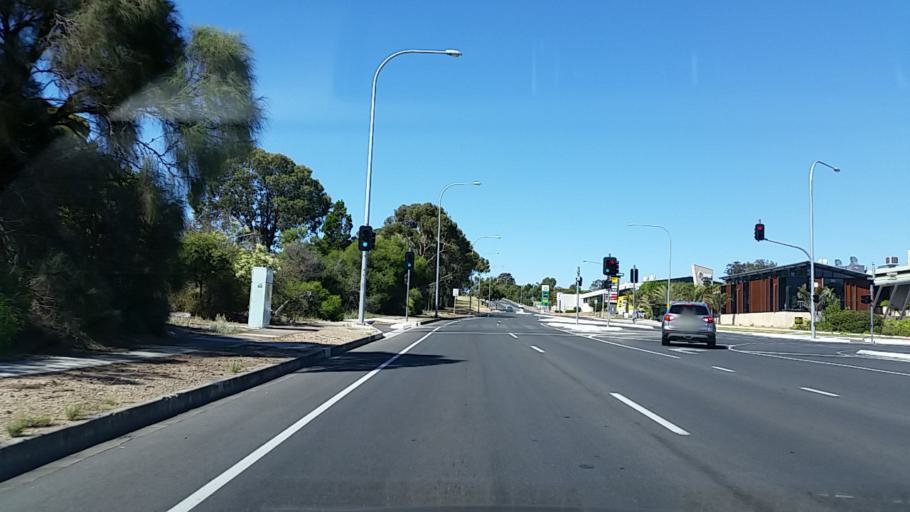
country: AU
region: South Australia
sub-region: Tea Tree Gully
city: Hope Valley
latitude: -34.8064
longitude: 138.7000
